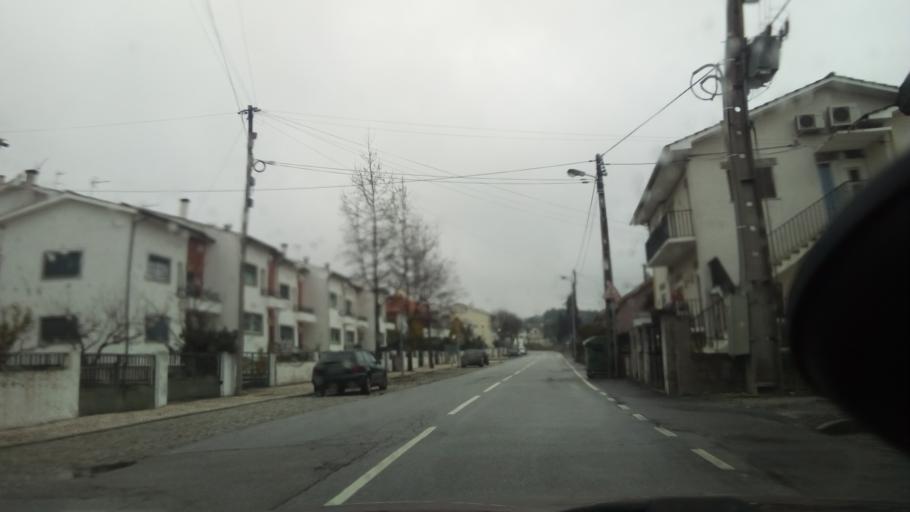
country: PT
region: Viseu
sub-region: Viseu
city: Rio de Loba
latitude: 40.6538
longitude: -7.8732
